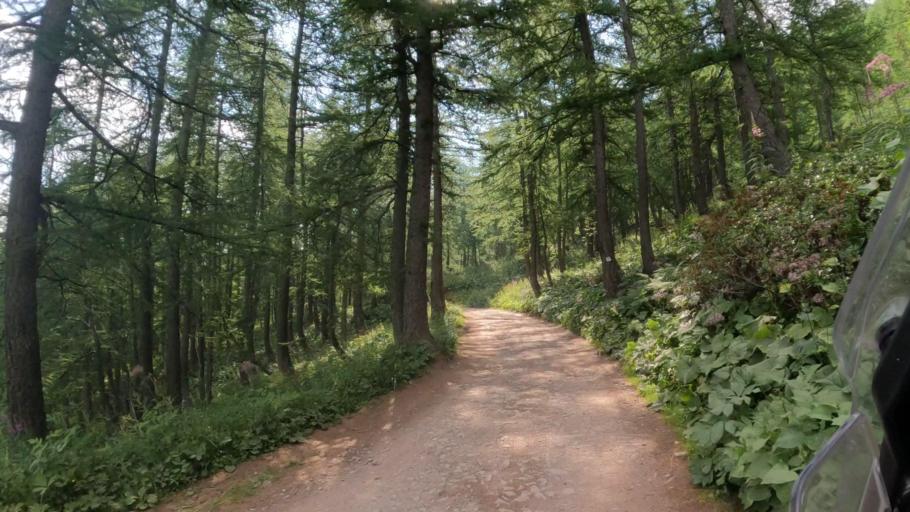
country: IT
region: Piedmont
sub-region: Provincia di Cuneo
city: Briga Alta
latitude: 44.1268
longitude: 7.6817
